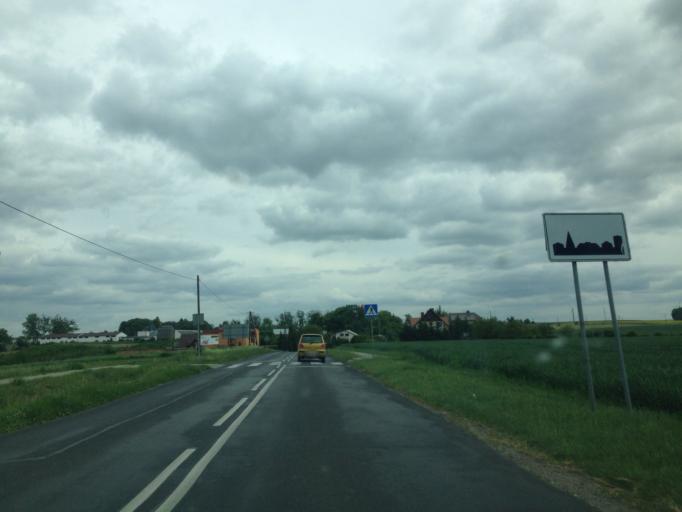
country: PL
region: Kujawsko-Pomorskie
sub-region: Powiat brodnicki
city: Brodnica
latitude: 53.2484
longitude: 19.4545
